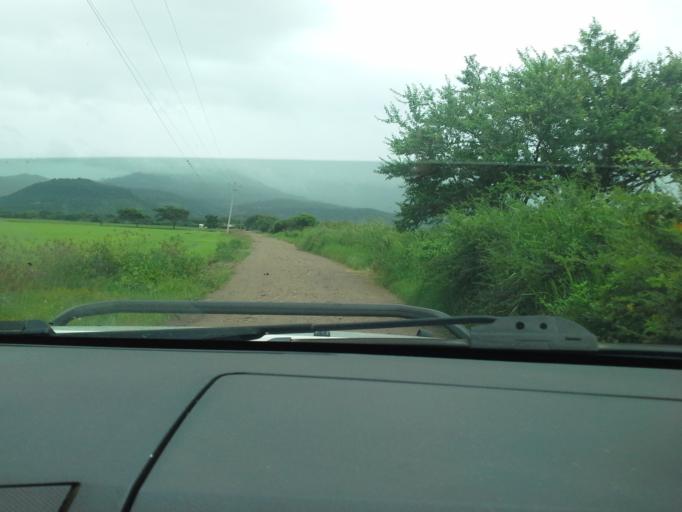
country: NI
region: Matagalpa
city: Ciudad Dario
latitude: 12.8588
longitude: -86.1838
